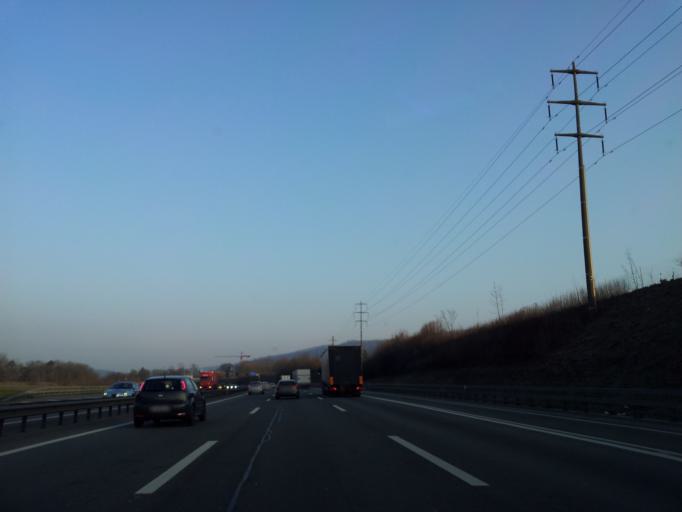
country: CH
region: Aargau
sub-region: Bezirk Baden
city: Neuenhof
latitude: 47.4502
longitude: 8.3384
